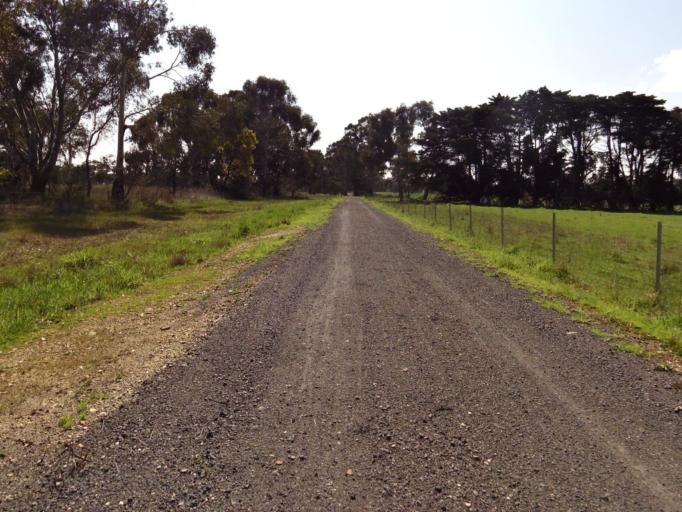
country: AU
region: Victoria
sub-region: Murrindindi
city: Alexandra
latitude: -37.1247
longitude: 145.5992
